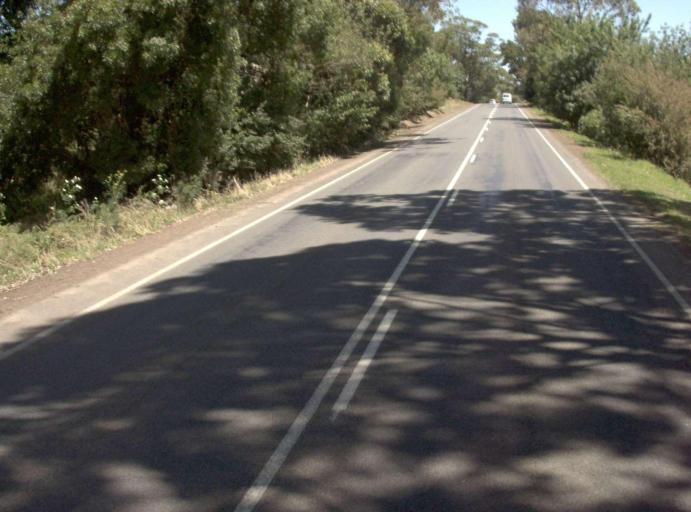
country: AU
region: Victoria
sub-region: Baw Baw
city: Warragul
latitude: -37.9725
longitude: 145.9506
